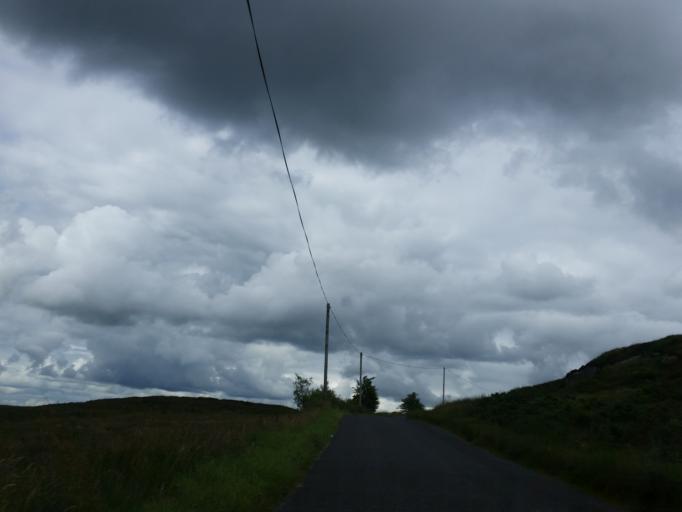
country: IE
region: Ulster
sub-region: County Monaghan
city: Clones
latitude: 54.2683
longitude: -7.2752
